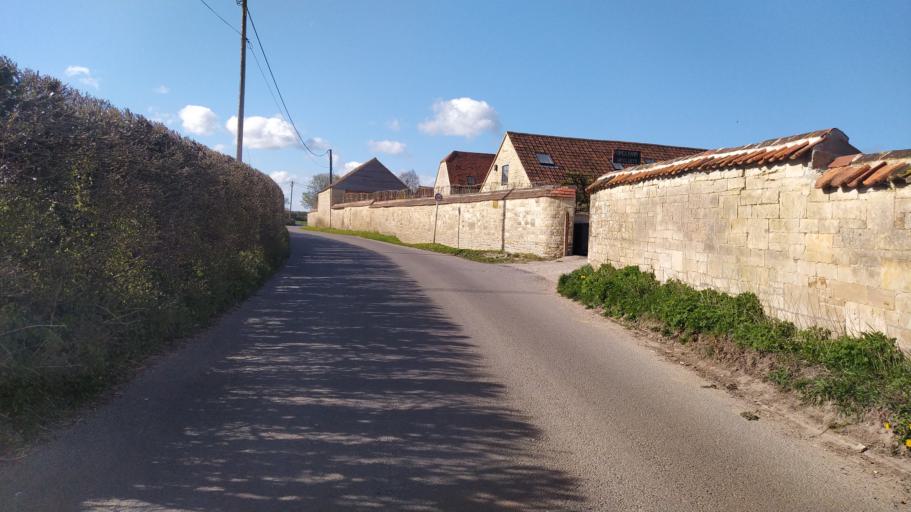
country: GB
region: England
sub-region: Dorset
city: Sturminster Newton
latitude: 50.9635
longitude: -2.3260
